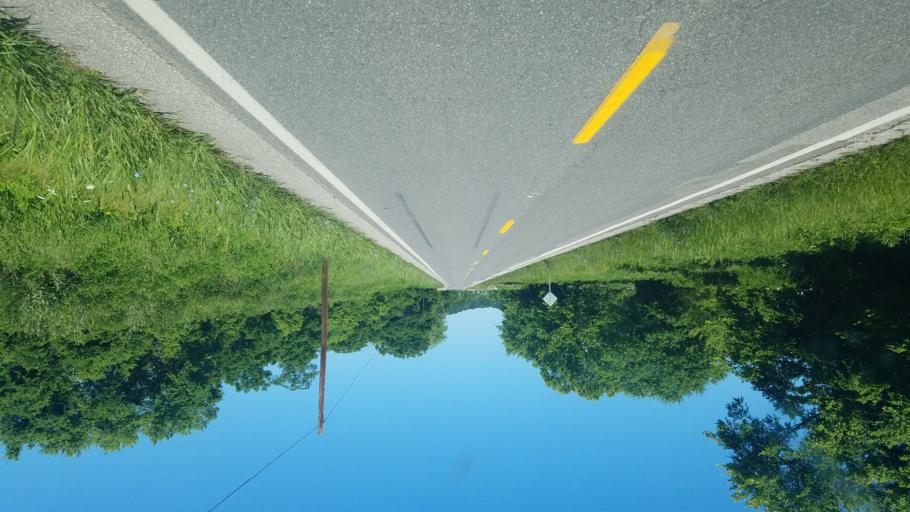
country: US
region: West Virginia
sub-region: Cabell County
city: Lesage
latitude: 38.5874
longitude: -82.2049
